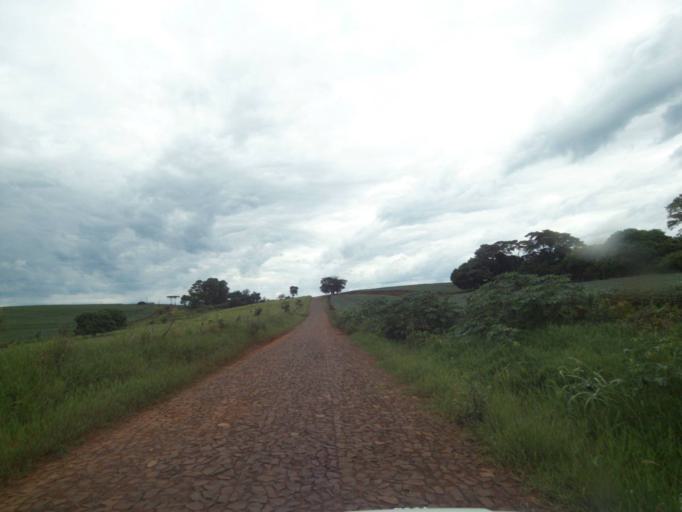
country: BR
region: Parana
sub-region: Guaraniacu
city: Guaraniacu
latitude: -24.9253
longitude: -52.9382
